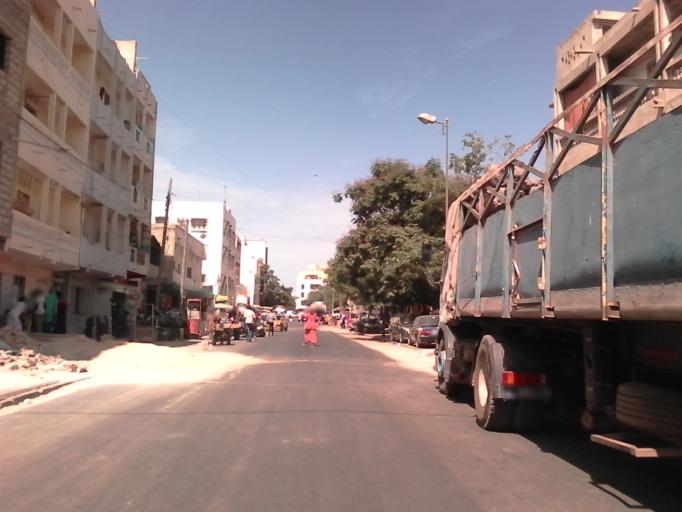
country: SN
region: Dakar
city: Grand Dakar
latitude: 14.7069
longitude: -17.4570
